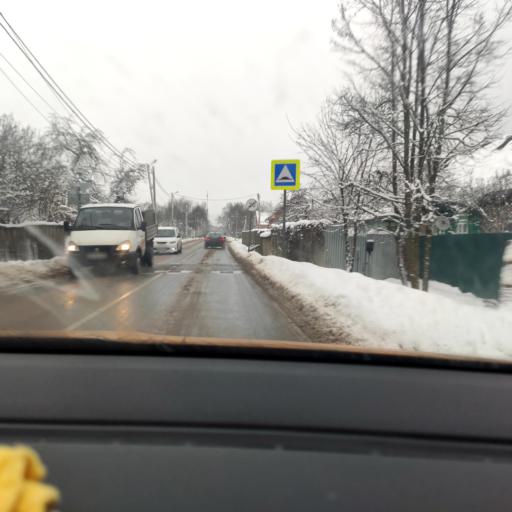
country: RU
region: Moskovskaya
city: Yershovo
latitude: 55.7531
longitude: 36.8708
